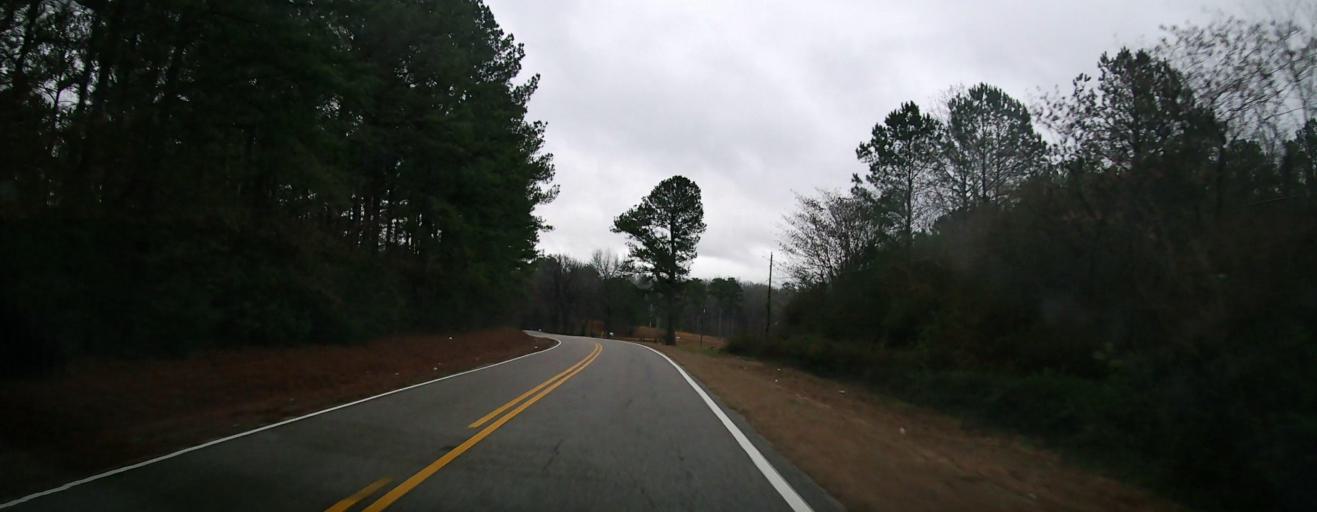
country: US
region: Alabama
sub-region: Bibb County
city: Centreville
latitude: 32.9707
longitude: -87.1450
